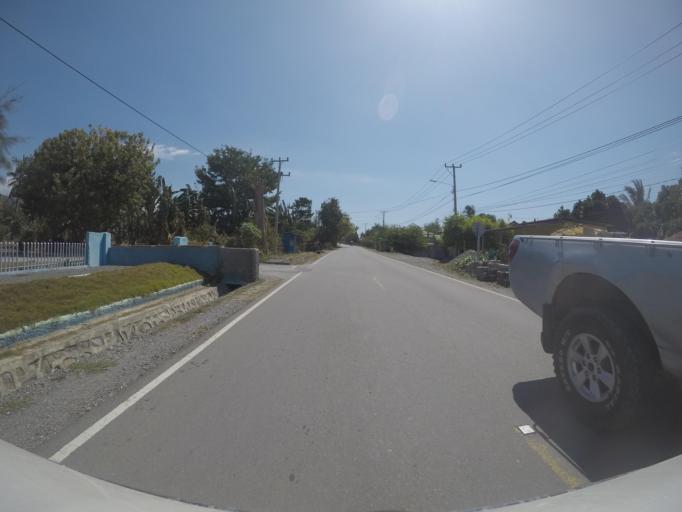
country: TL
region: Liquica
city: Liquica
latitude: -8.5893
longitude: 125.3466
